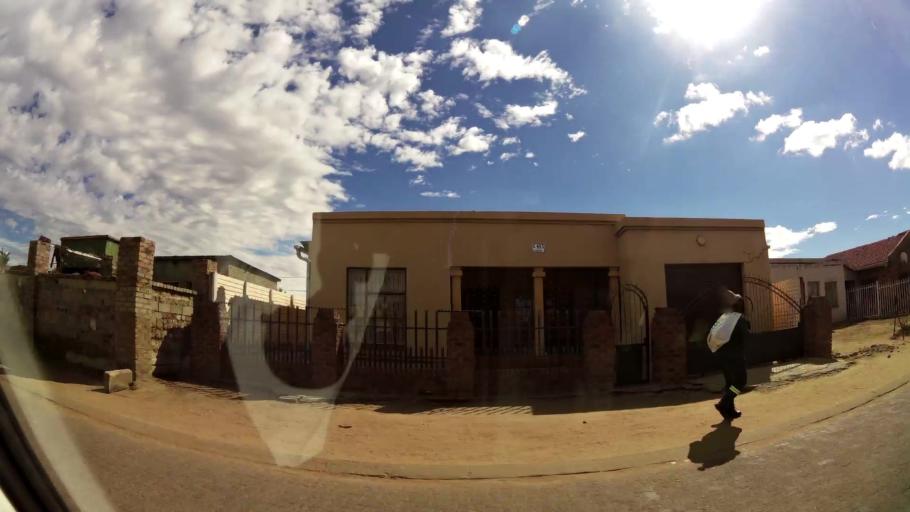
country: ZA
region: Limpopo
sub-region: Waterberg District Municipality
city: Bela-Bela
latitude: -24.8811
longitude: 28.3174
